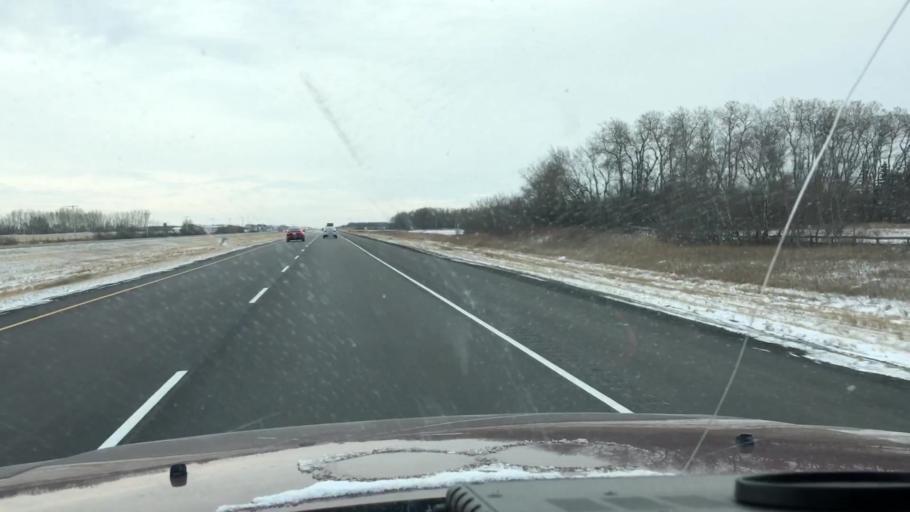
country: CA
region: Saskatchewan
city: Saskatoon
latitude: 51.9762
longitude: -106.5570
